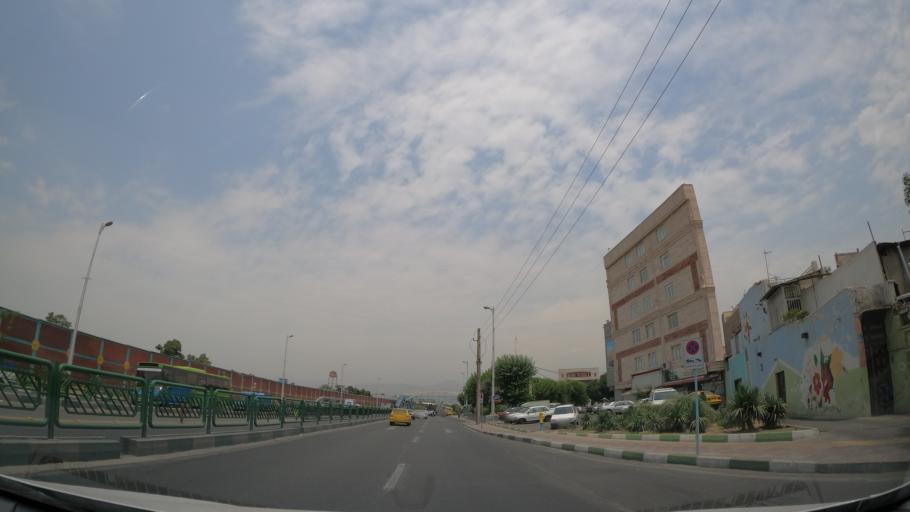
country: IR
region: Tehran
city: Tehran
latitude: 35.6874
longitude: 51.3411
